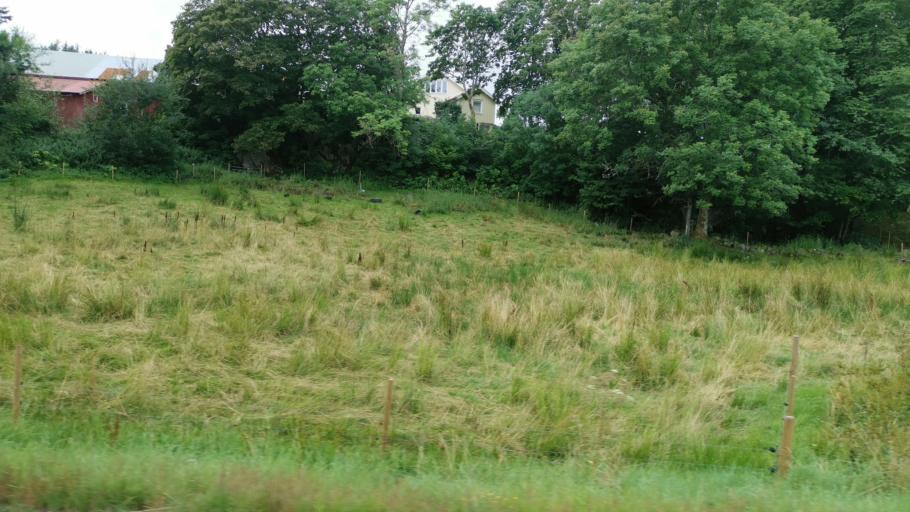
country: SE
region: Vaestra Goetaland
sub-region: Sotenas Kommun
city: Hunnebostrand
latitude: 58.4806
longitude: 11.3972
